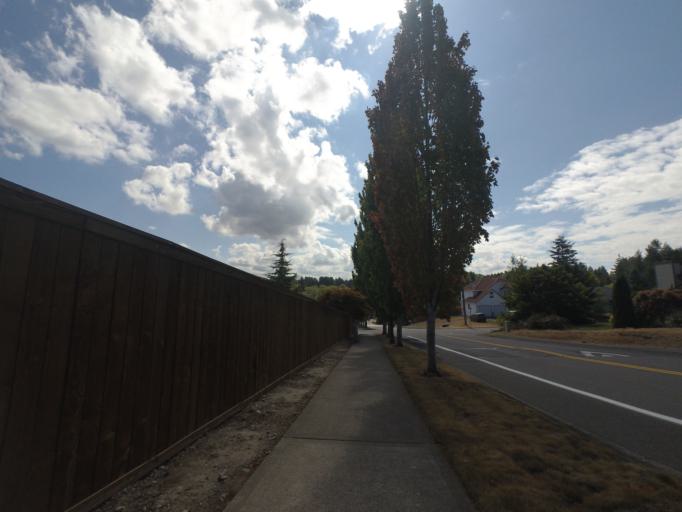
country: US
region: Washington
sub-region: Pierce County
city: Fircrest
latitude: 47.2086
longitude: -122.5159
